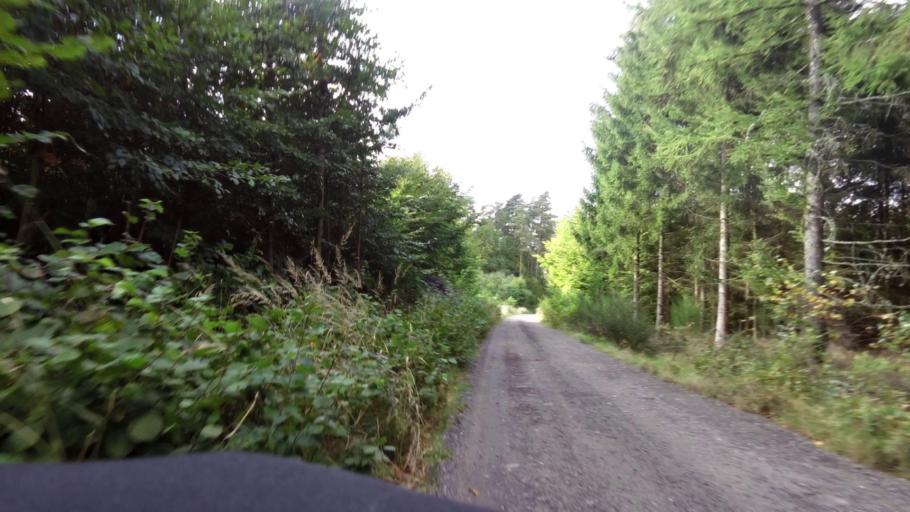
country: PL
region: West Pomeranian Voivodeship
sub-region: Koszalin
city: Koszalin
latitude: 54.0534
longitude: 16.1321
